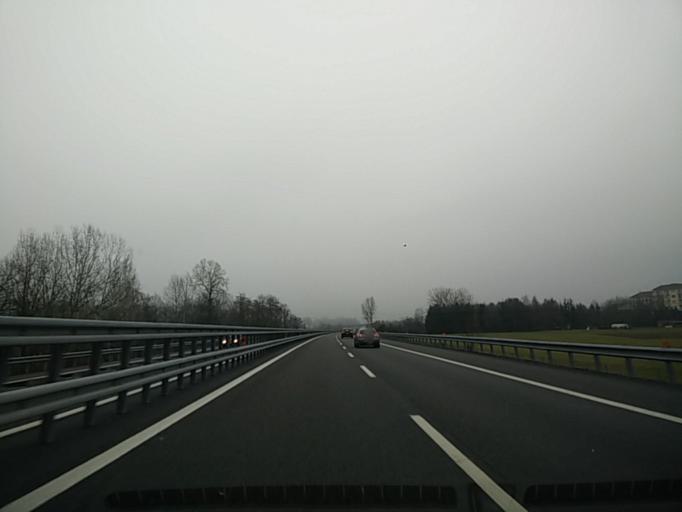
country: IT
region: Piedmont
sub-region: Provincia di Asti
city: Villafranca d'Asti
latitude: 44.9127
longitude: 8.0422
